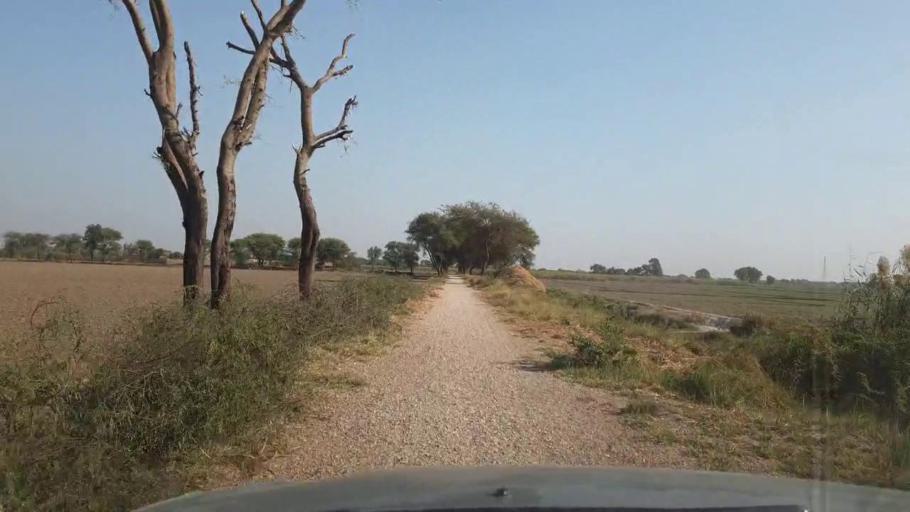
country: PK
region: Sindh
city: Tando Muhammad Khan
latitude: 25.0889
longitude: 68.5711
